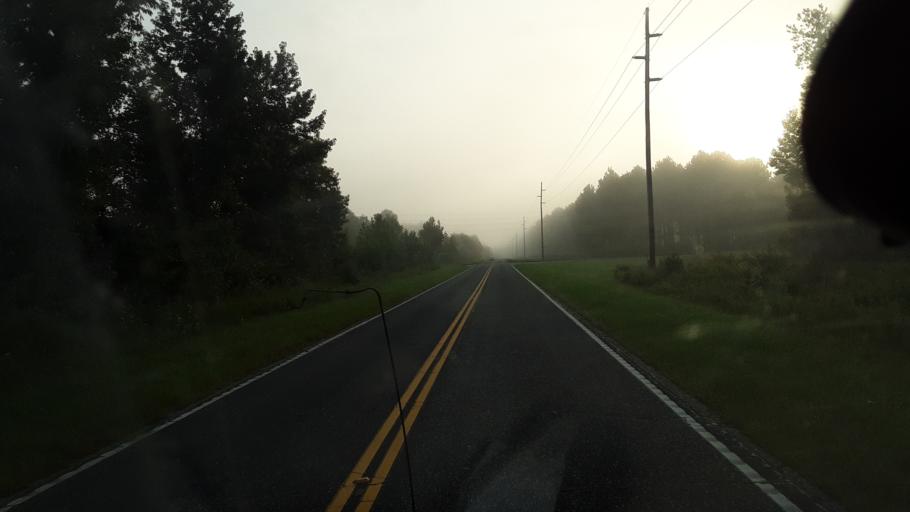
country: US
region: South Carolina
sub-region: Williamsburg County
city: Kingstree
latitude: 33.8245
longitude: -79.9509
